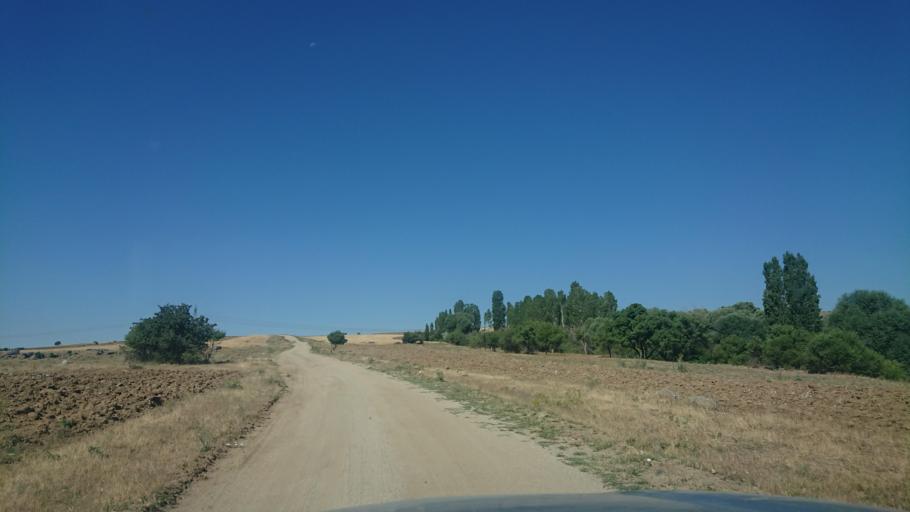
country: TR
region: Aksaray
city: Sariyahsi
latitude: 38.9427
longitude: 33.8748
